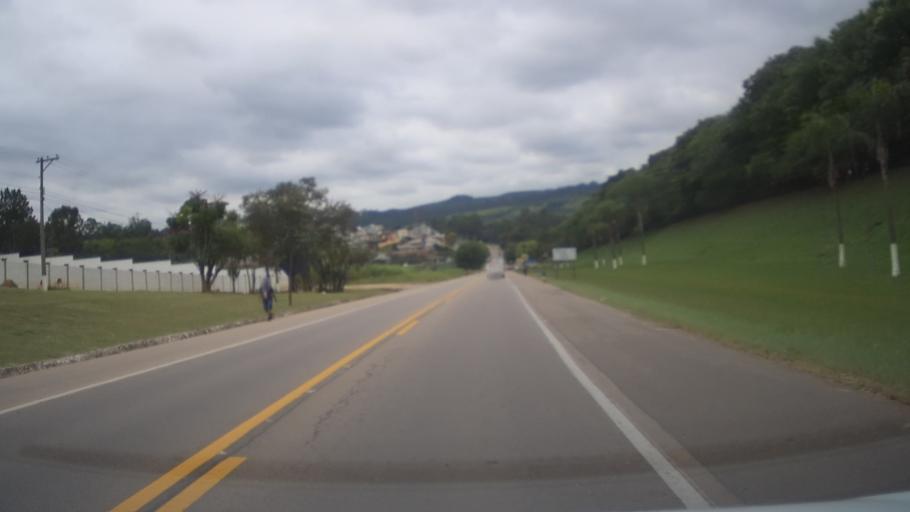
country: BR
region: Sao Paulo
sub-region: Louveira
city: Louveira
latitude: -23.0716
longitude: -46.9519
